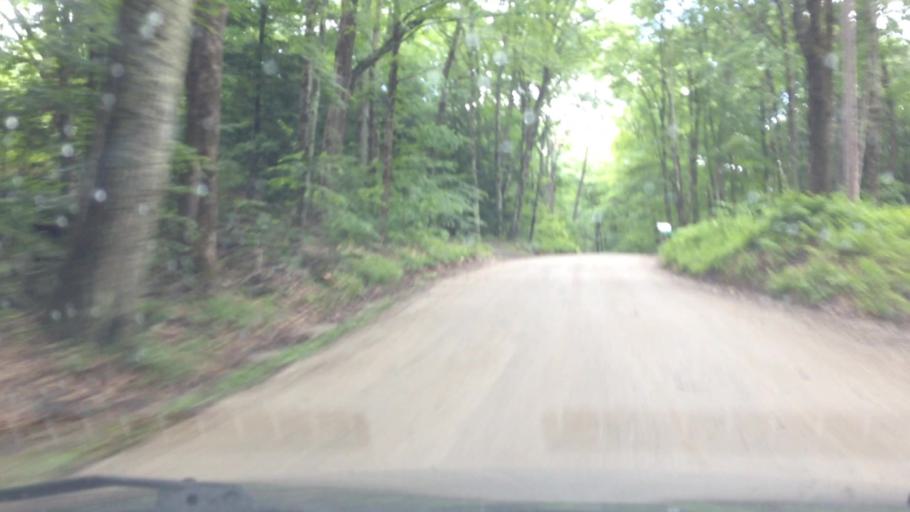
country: US
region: New Hampshire
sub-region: Cheshire County
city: Marlborough
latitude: 42.8954
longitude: -72.1876
